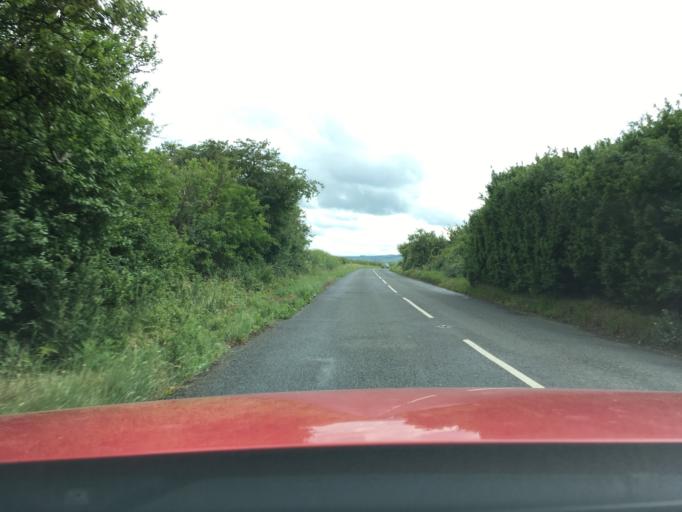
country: GB
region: England
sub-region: Worcestershire
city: Evesham
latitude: 52.0388
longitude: -1.9632
